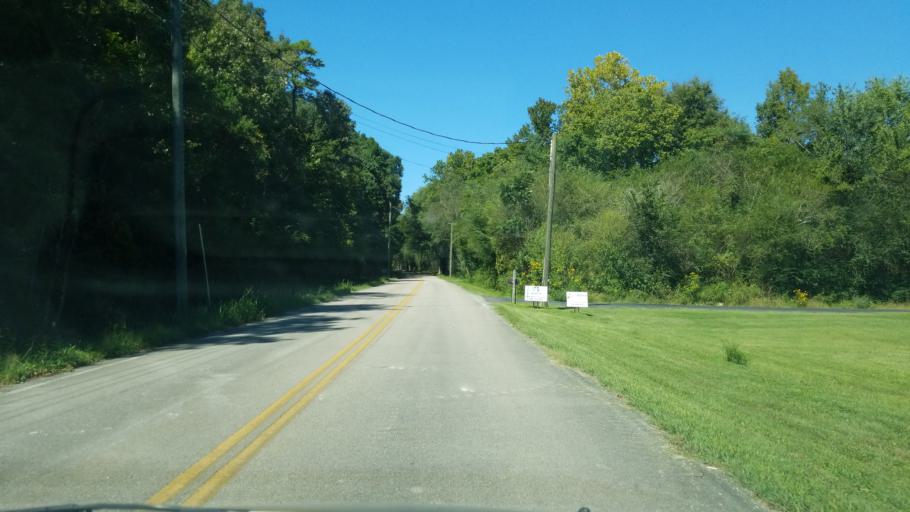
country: US
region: Tennessee
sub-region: Hamilton County
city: Harrison
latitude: 35.1026
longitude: -85.0857
